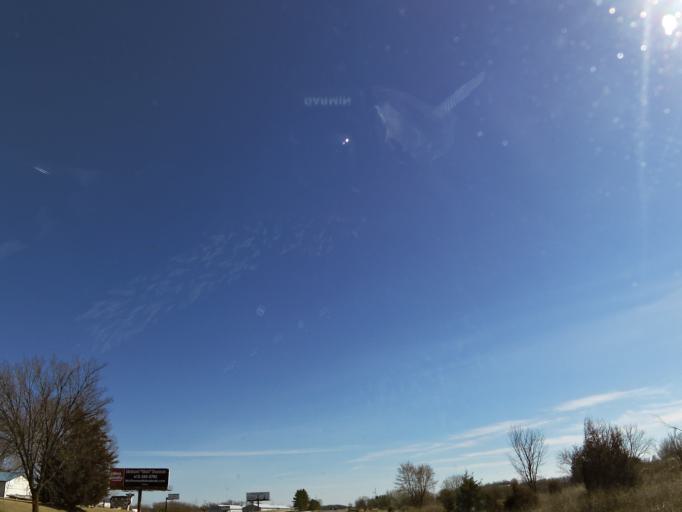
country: US
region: Minnesota
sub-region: Wright County
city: Buffalo
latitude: 45.1436
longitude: -93.8357
